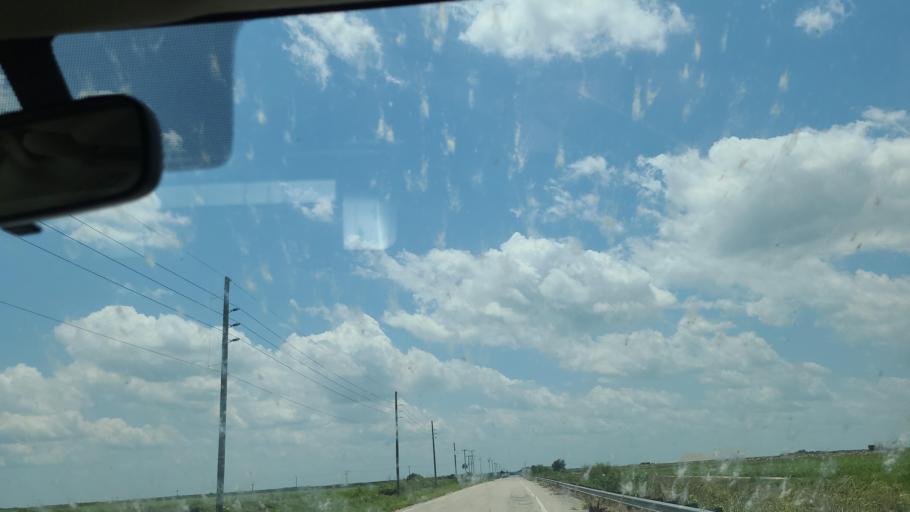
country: US
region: Florida
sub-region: Glades County
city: Buckhead Ridge
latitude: 27.1751
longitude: -81.0943
